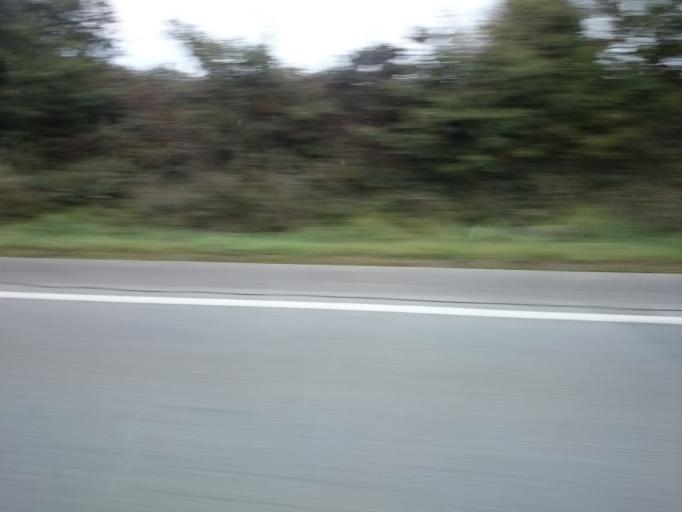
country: FR
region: Brittany
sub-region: Departement du Morbihan
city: Nostang
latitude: 47.7714
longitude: -3.1769
